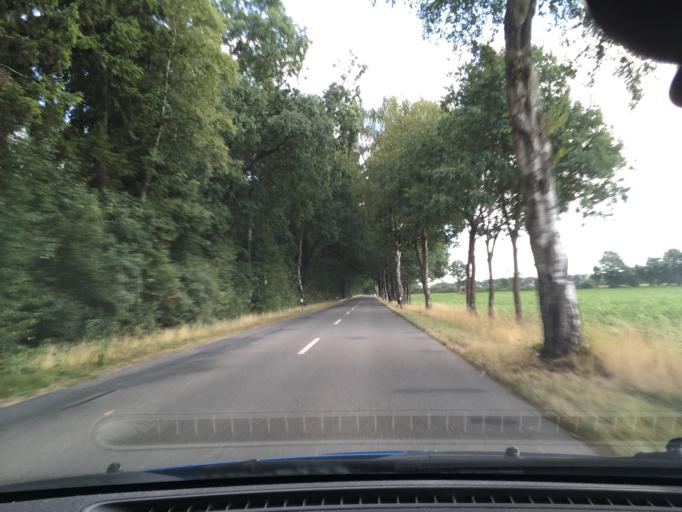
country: DE
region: Lower Saxony
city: Wriedel
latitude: 53.0435
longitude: 10.2651
